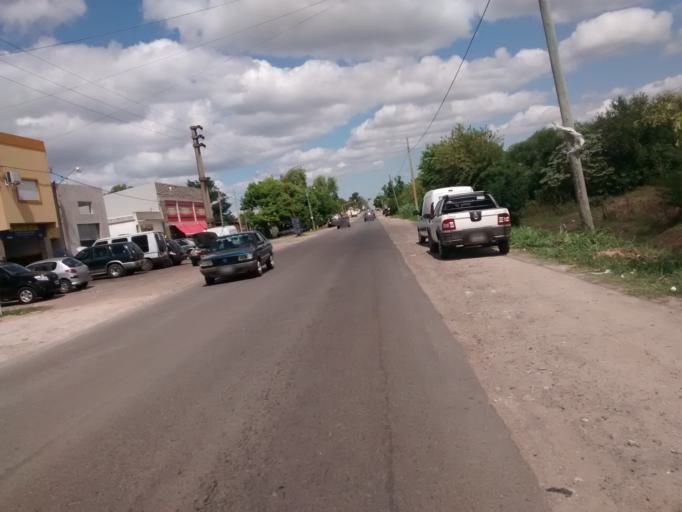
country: AR
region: Buenos Aires
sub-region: Partido de La Plata
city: La Plata
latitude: -34.9582
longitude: -57.9611
